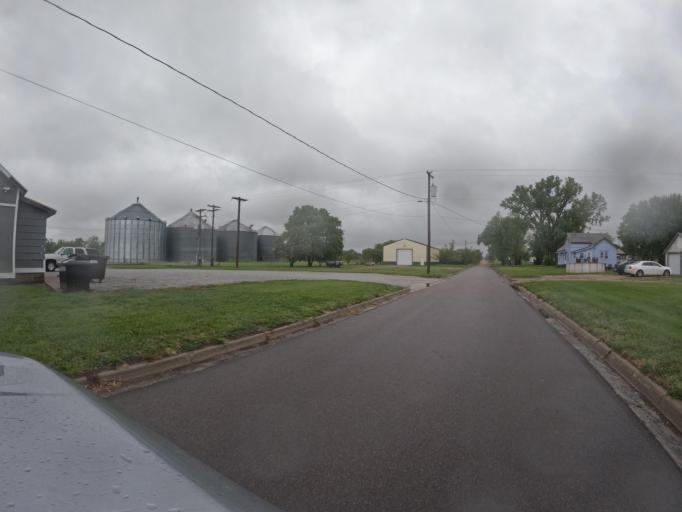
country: US
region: Nebraska
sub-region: Clay County
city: Harvard
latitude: 40.6181
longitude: -98.0990
